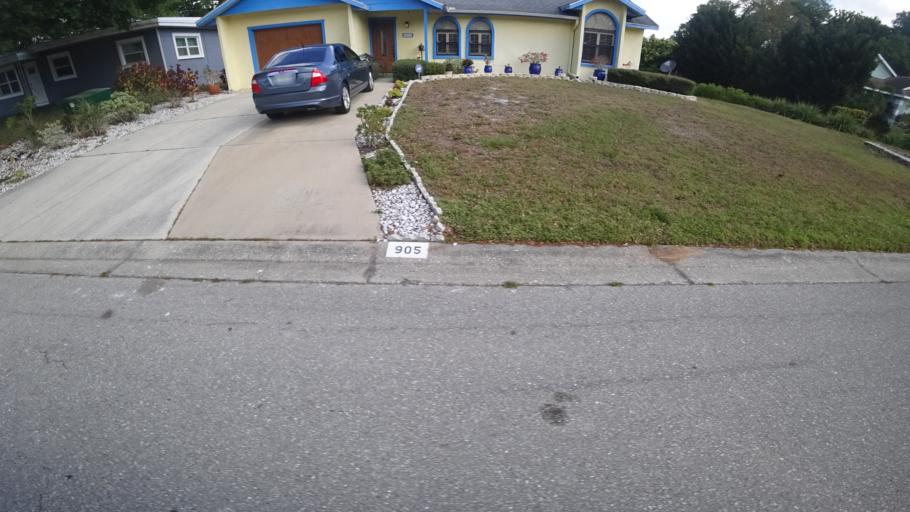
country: US
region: Florida
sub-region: Manatee County
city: Whitfield
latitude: 27.4194
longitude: -82.5719
